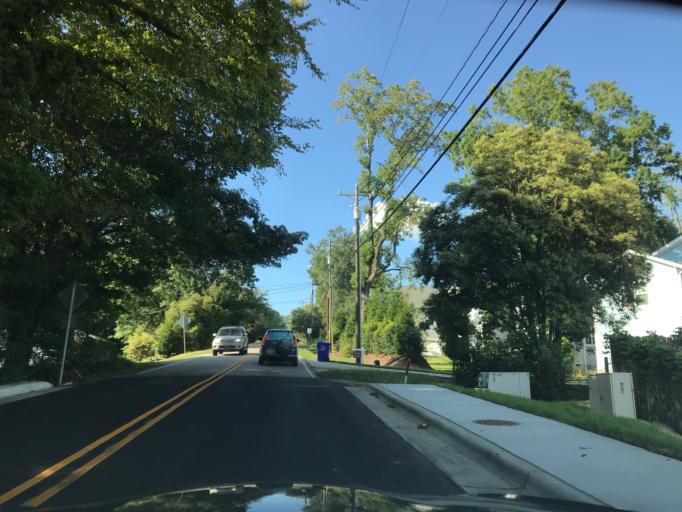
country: US
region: North Carolina
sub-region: Orange County
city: Carrboro
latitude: 35.9038
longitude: -79.0725
